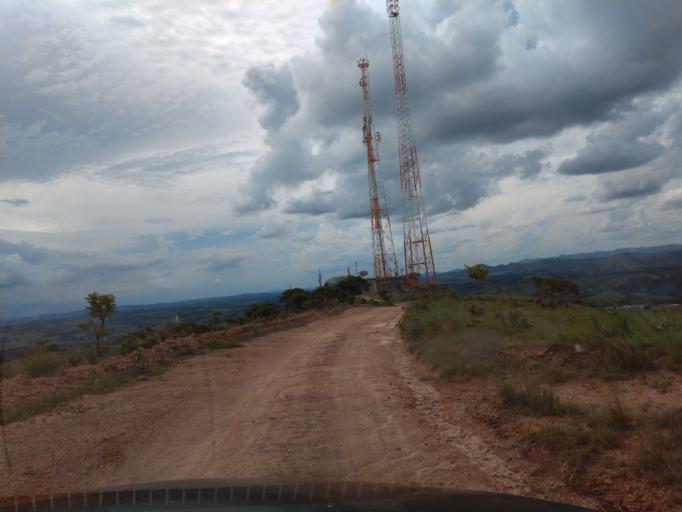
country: BR
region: Minas Gerais
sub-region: Lavras
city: Lavras
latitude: -21.5282
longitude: -44.9028
